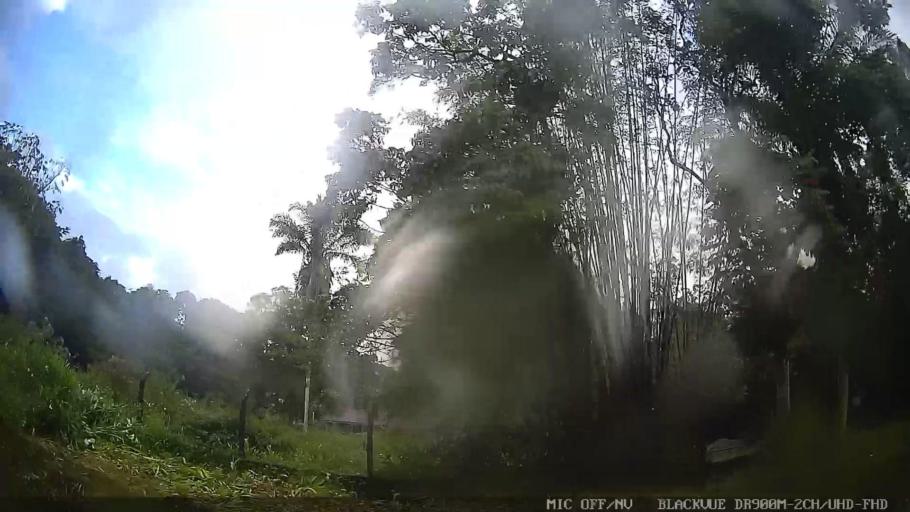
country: BR
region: Sao Paulo
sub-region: Peruibe
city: Peruibe
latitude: -24.2218
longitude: -46.9199
